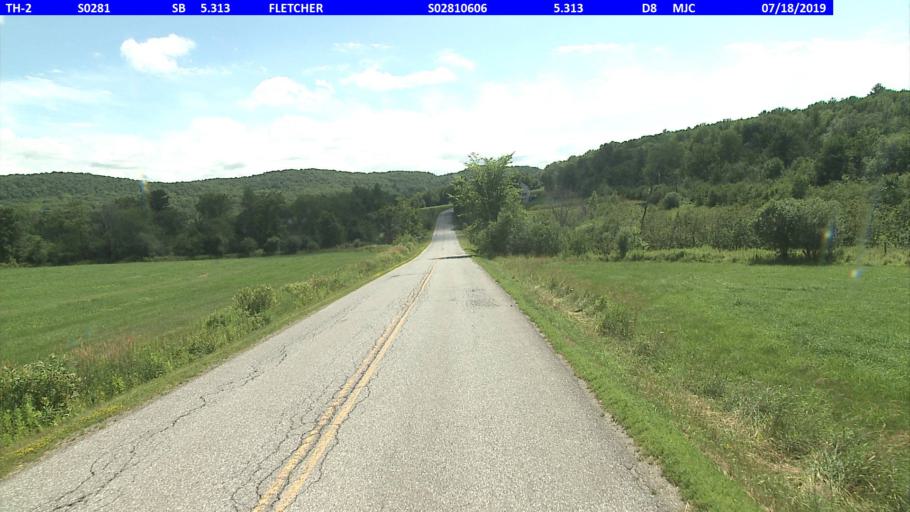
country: US
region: Vermont
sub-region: Franklin County
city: Saint Albans
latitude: 44.7426
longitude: -72.9476
